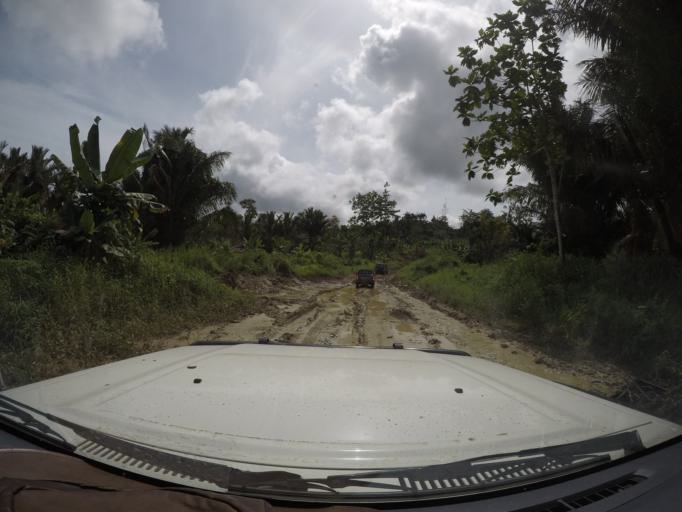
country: PG
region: Gulf
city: Kerema
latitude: -7.9955
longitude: 145.8294
